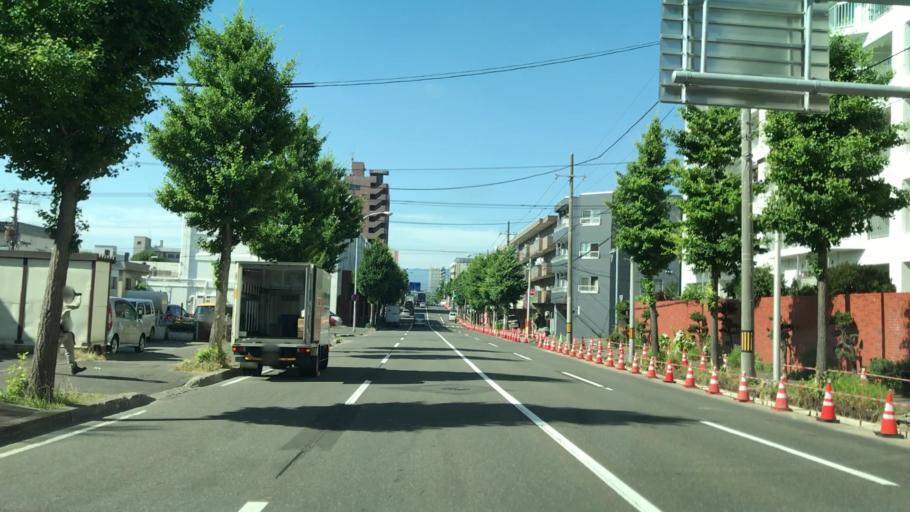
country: JP
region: Hokkaido
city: Sapporo
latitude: 43.0514
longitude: 141.4116
